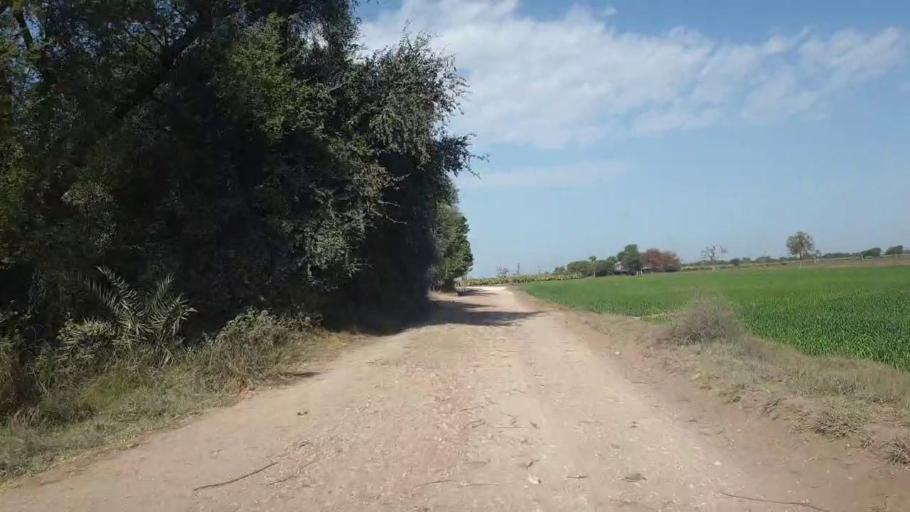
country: PK
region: Sindh
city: Sakrand
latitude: 25.9773
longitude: 68.3391
